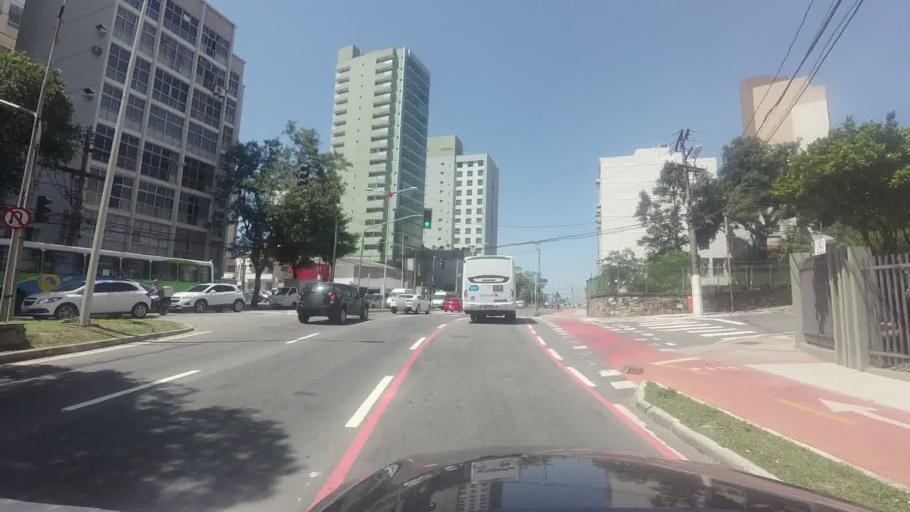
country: BR
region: Espirito Santo
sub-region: Vila Velha
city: Vila Velha
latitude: -20.2978
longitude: -40.2915
